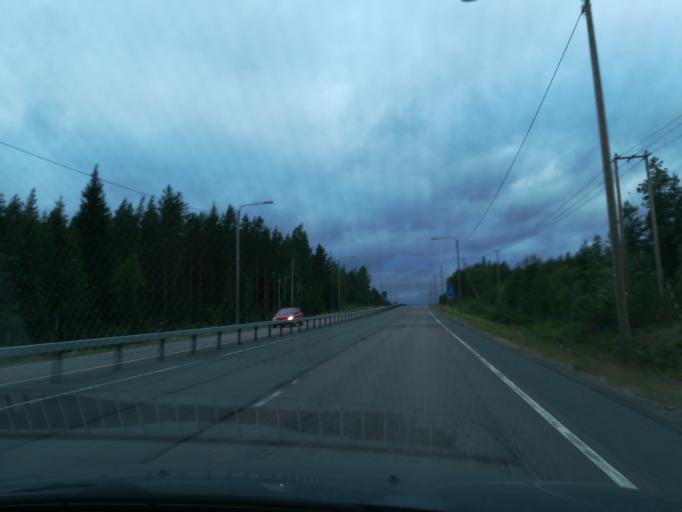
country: FI
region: Southern Savonia
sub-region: Mikkeli
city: Ristiina
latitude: 61.4068
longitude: 27.3500
